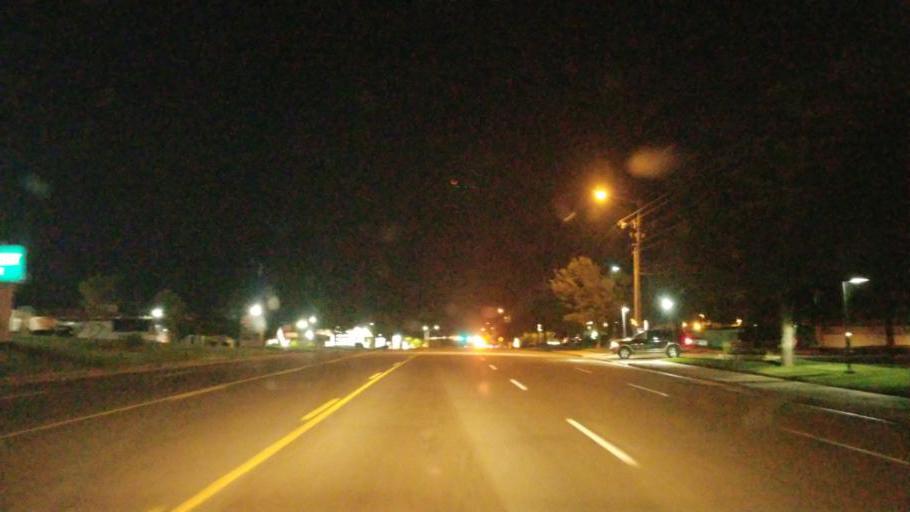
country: US
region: Texas
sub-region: Potter County
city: Amarillo
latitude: 35.1955
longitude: -101.9218
